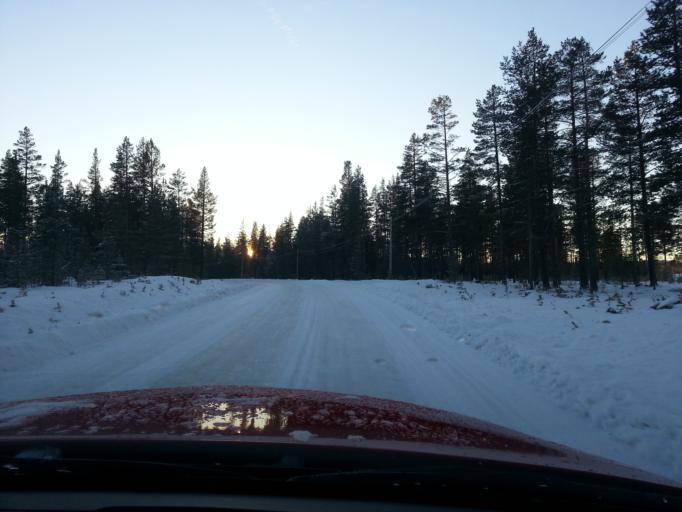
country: SE
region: Jaemtland
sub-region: Harjedalens Kommun
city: Sveg
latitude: 62.3741
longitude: 13.4680
